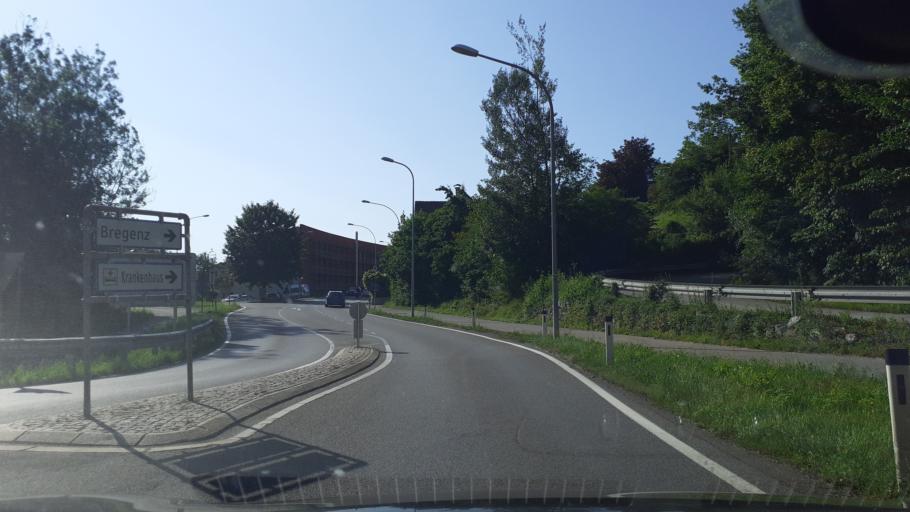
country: AT
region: Vorarlberg
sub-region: Politischer Bezirk Bregenz
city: Lauterach
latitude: 47.4883
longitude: 9.7442
